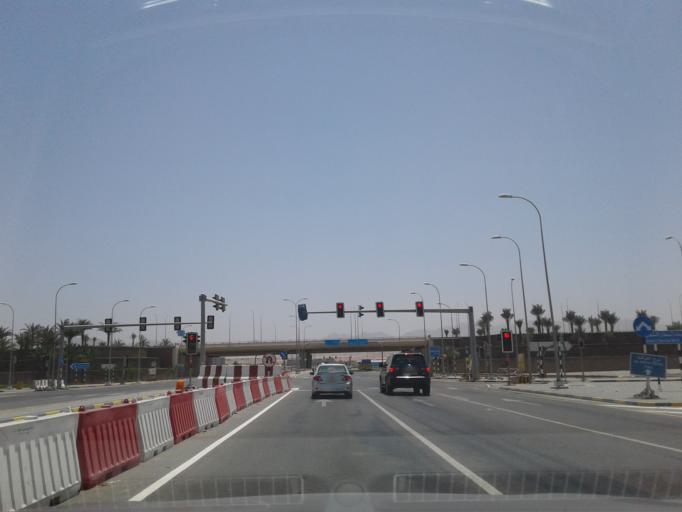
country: OM
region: Muhafazat Masqat
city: Bawshar
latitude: 23.6049
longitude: 58.3112
